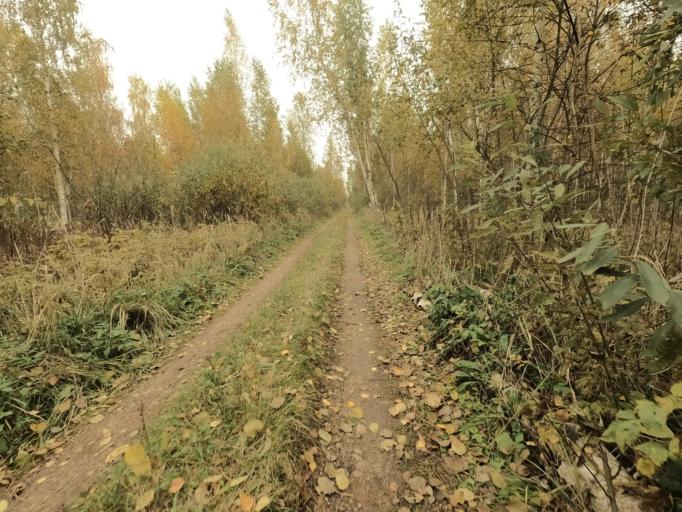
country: RU
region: Novgorod
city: Pankovka
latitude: 58.8721
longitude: 30.9376
